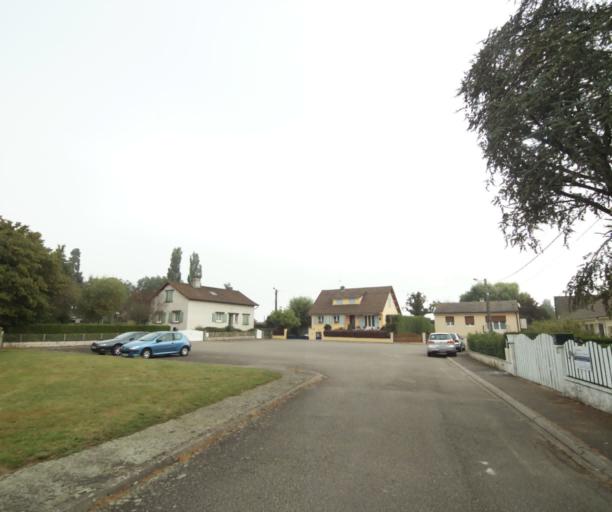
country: FR
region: Bourgogne
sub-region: Departement de Saone-et-Loire
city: Charolles
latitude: 46.4355
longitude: 4.2663
